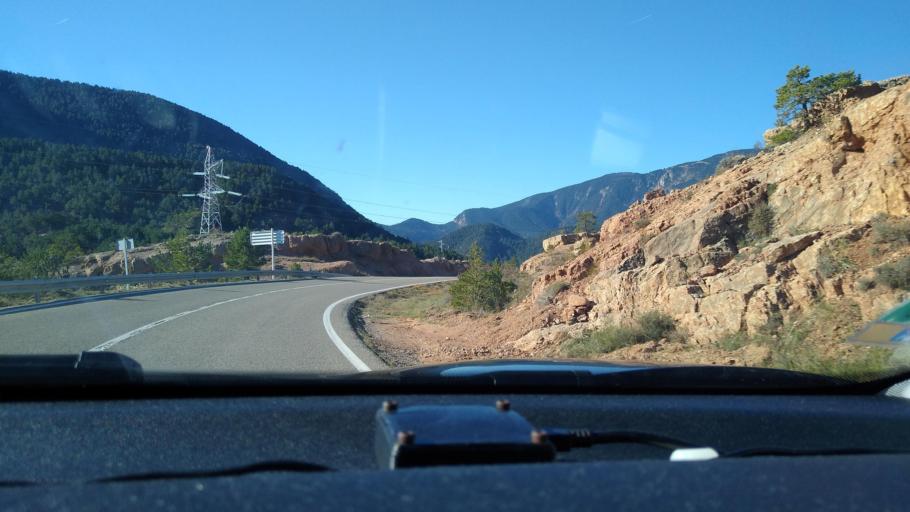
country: ES
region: Catalonia
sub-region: Provincia de Barcelona
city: Saldes
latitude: 42.2169
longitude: 1.7190
